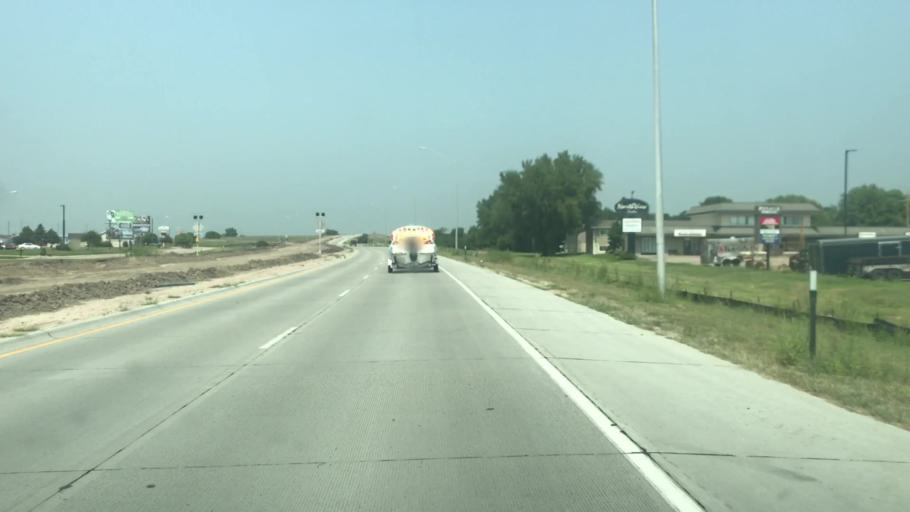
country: US
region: Nebraska
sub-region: Hall County
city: Grand Island
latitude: 40.9467
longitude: -98.3835
